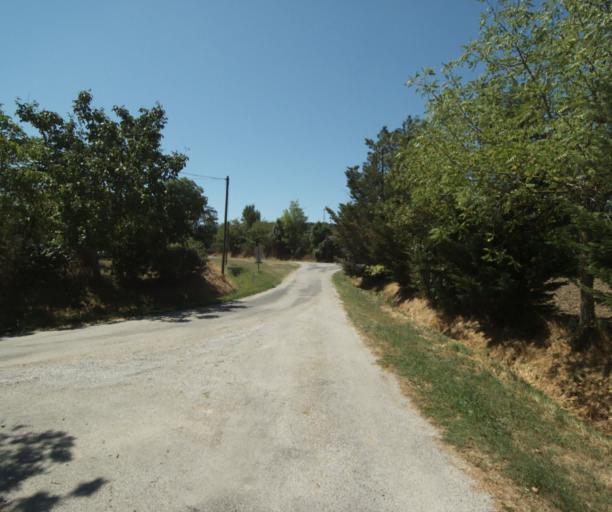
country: FR
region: Midi-Pyrenees
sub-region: Departement de la Haute-Garonne
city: Saint-Felix-Lauragais
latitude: 43.4662
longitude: 1.9305
